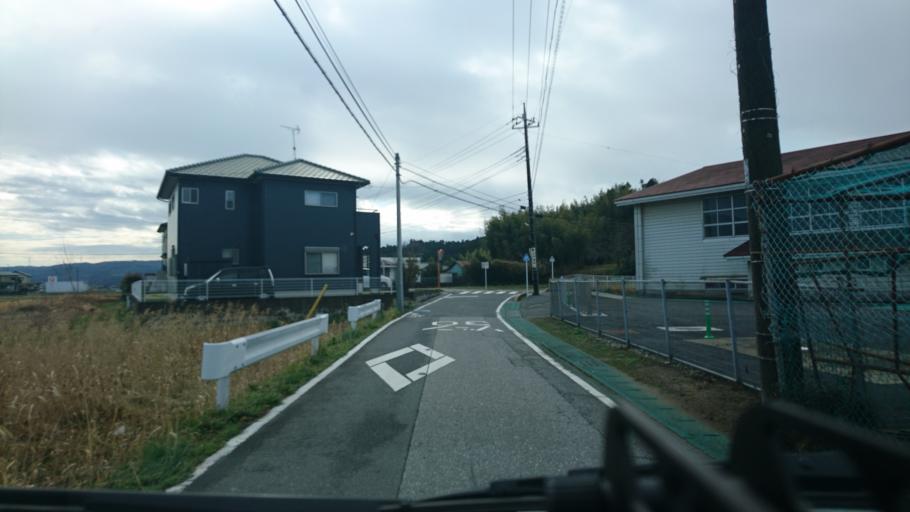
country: JP
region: Chiba
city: Kimitsu
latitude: 35.3046
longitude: 139.9592
